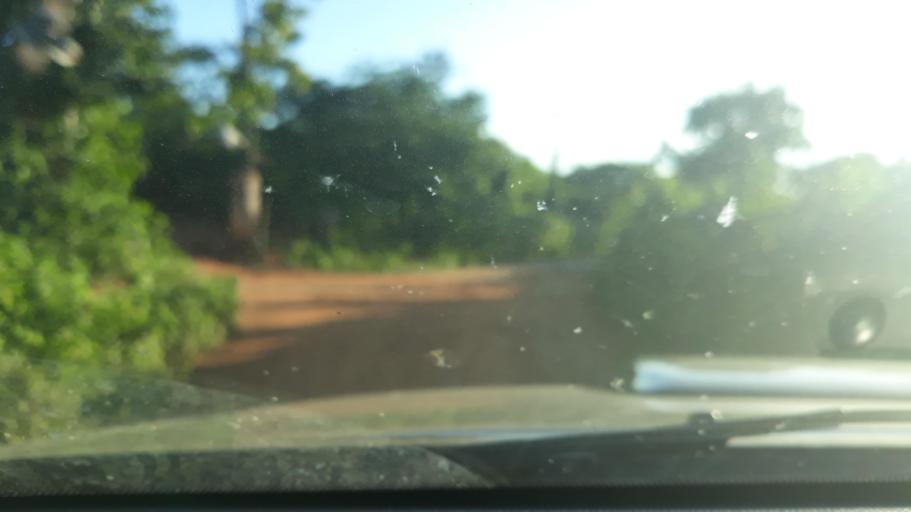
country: BR
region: Bahia
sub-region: Riacho De Santana
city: Riacho de Santana
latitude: -13.8423
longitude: -42.7379
